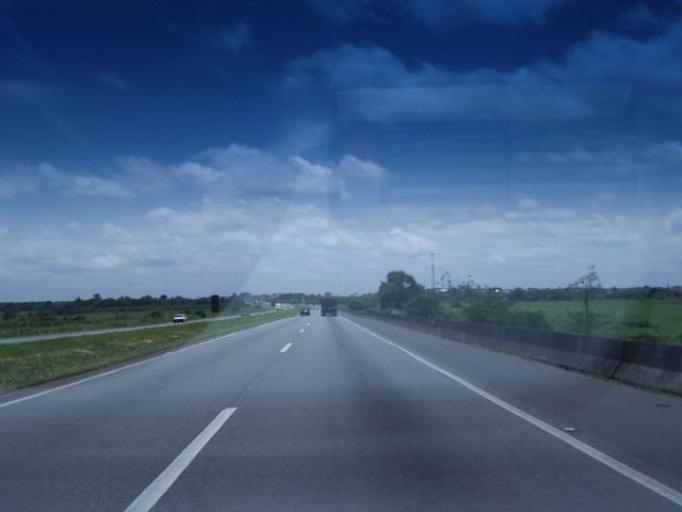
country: BR
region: Sao Paulo
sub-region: Registro
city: Registro
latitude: -24.4801
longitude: -47.8305
